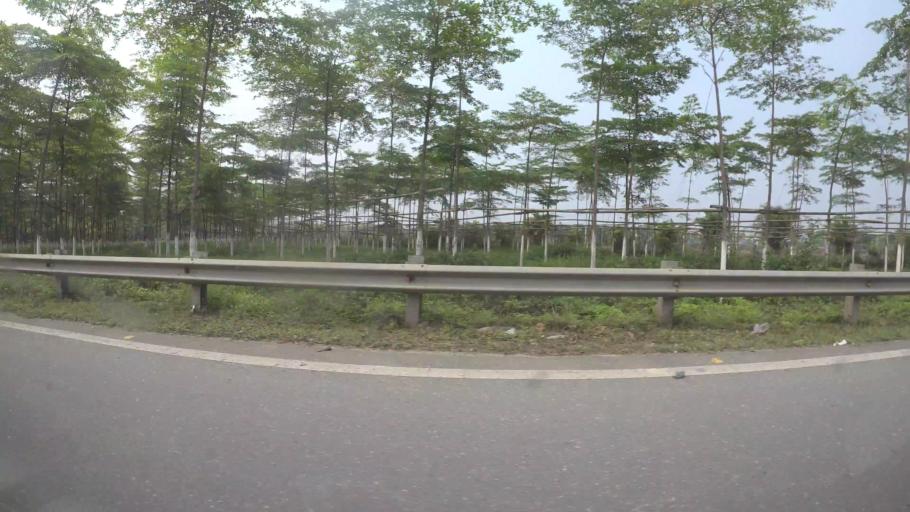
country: VN
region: Ha Noi
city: Lien Quan
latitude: 20.9932
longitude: 105.5245
